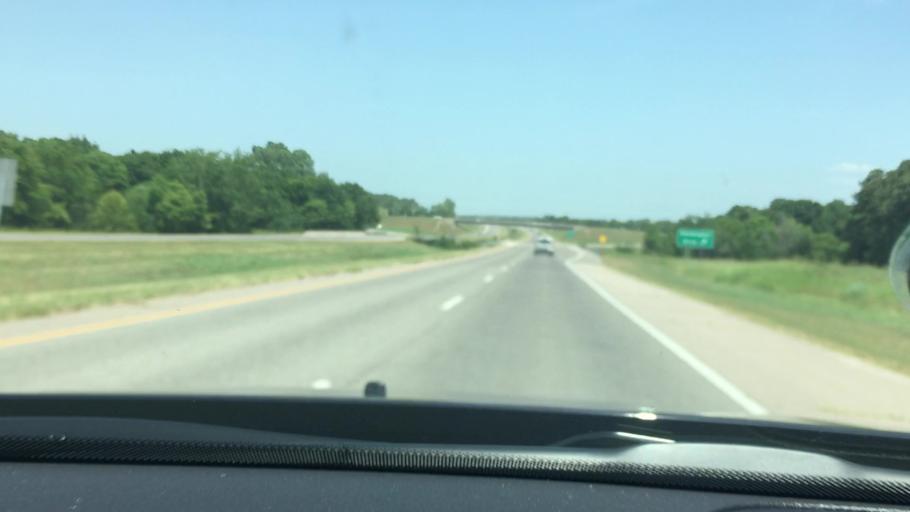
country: US
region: Oklahoma
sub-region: Pontotoc County
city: Ada
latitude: 34.7342
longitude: -96.6418
